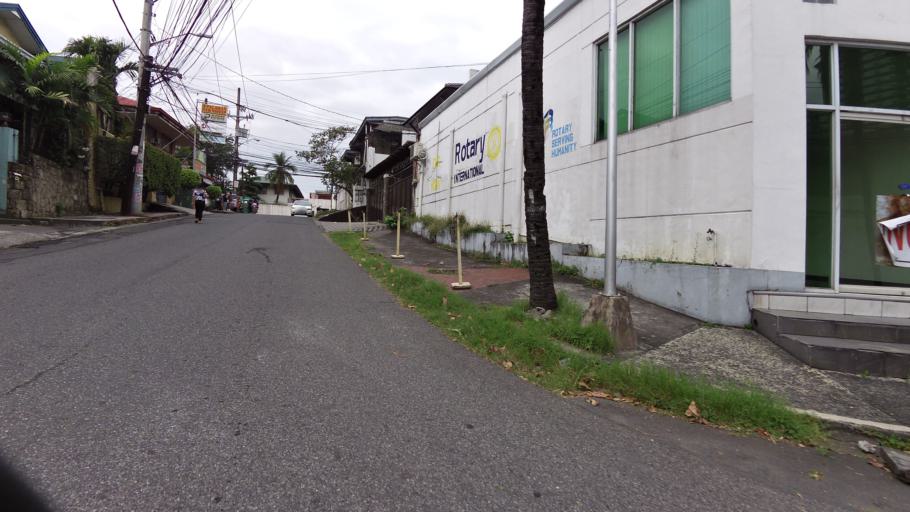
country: PH
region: Metro Manila
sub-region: Pasig
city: Pasig City
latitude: 14.5713
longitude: 121.0613
